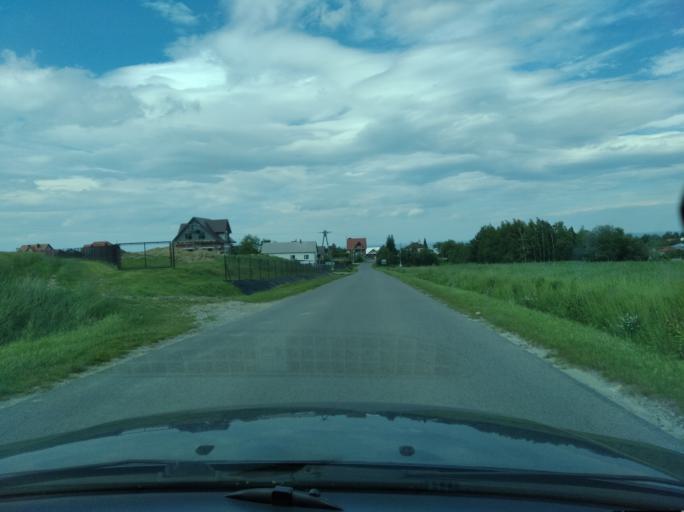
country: PL
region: Subcarpathian Voivodeship
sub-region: Powiat ropczycko-sedziszowski
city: Ropczyce
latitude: 50.0221
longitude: 21.6051
